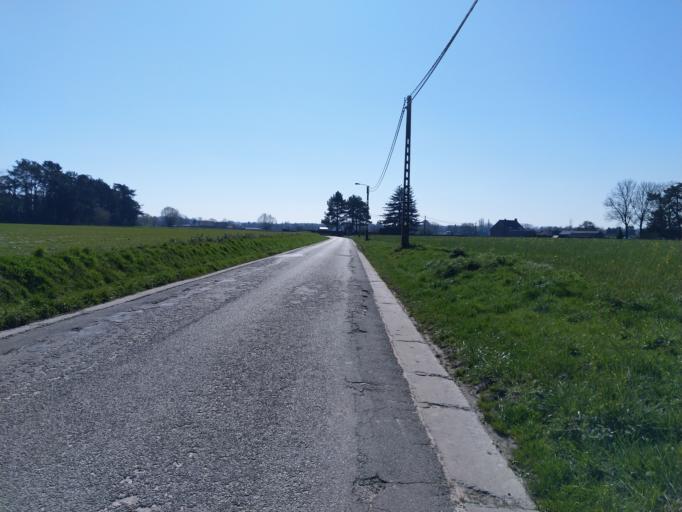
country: BE
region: Wallonia
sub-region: Province du Hainaut
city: Soignies
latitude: 50.5229
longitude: 4.0065
